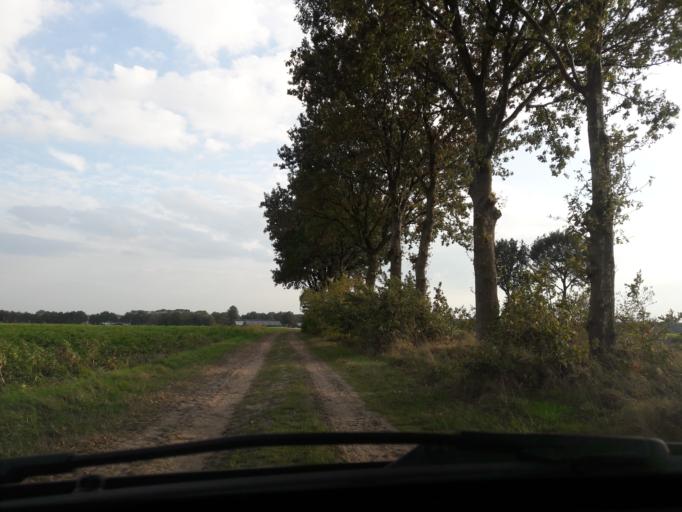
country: NL
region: Drenthe
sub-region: Gemeente Borger-Odoorn
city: Borger
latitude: 52.9529
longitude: 6.8136
